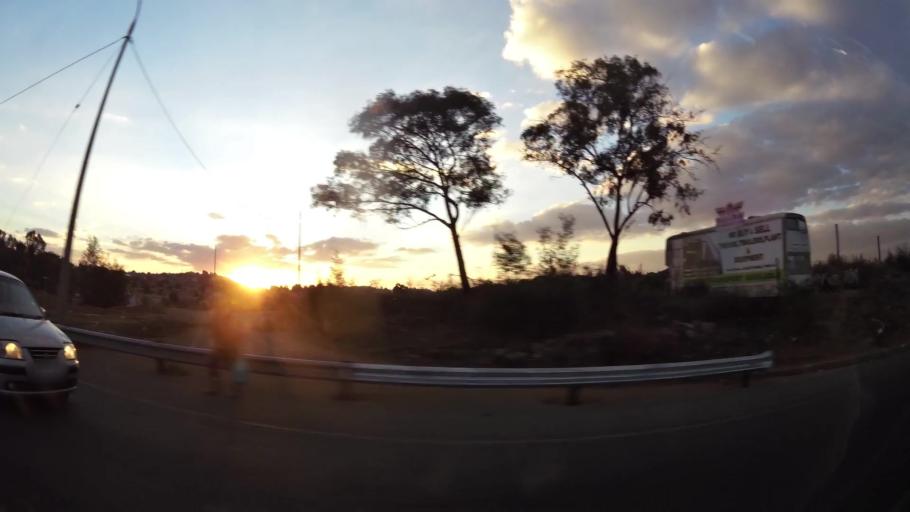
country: ZA
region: Gauteng
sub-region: West Rand District Municipality
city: Krugersdorp
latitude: -26.0762
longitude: 27.7962
